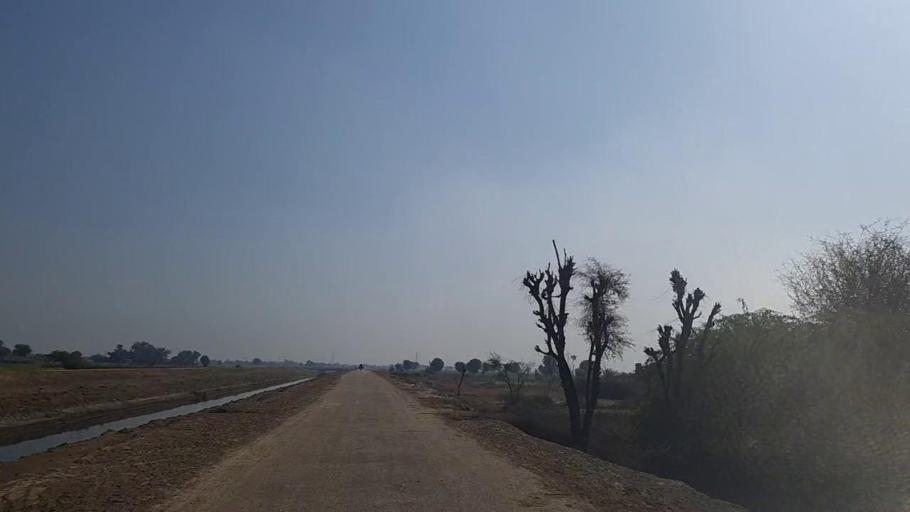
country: PK
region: Sindh
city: Shahpur Chakar
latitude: 26.1794
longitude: 68.5689
